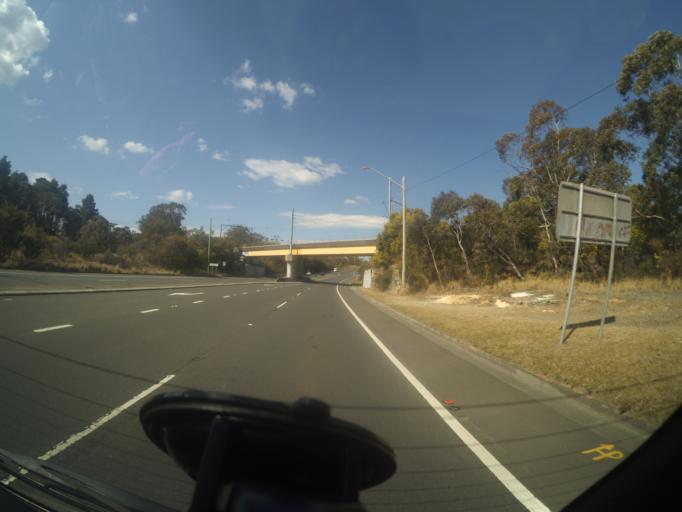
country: AU
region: New South Wales
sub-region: Blue Mountains Municipality
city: Leura
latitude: -33.7095
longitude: 150.3512
